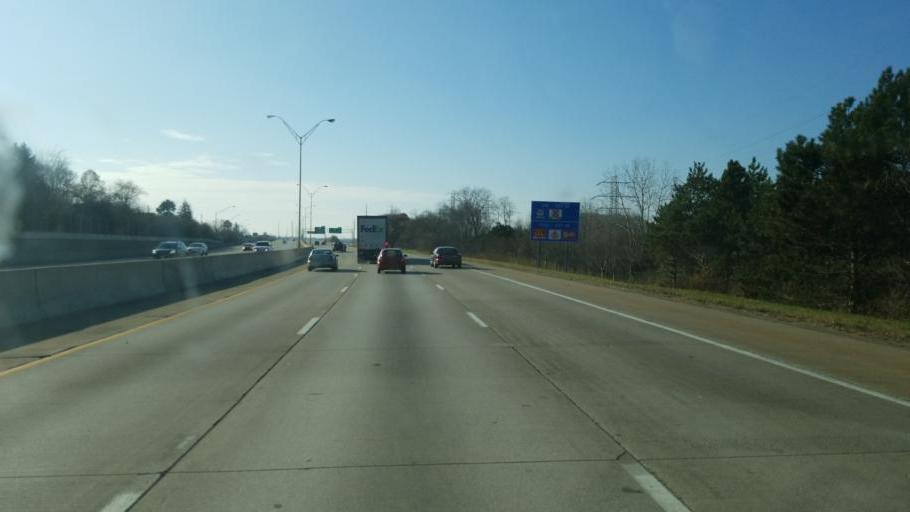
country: US
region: Ohio
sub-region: Summit County
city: Sawyerwood
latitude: 41.0640
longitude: -81.4491
